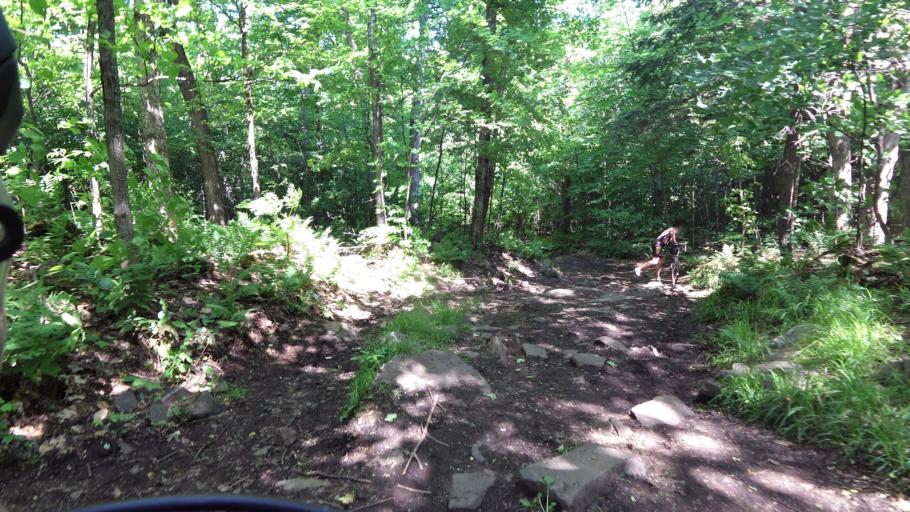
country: CA
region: Quebec
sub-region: Outaouais
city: Wakefield
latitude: 45.5385
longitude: -75.8742
